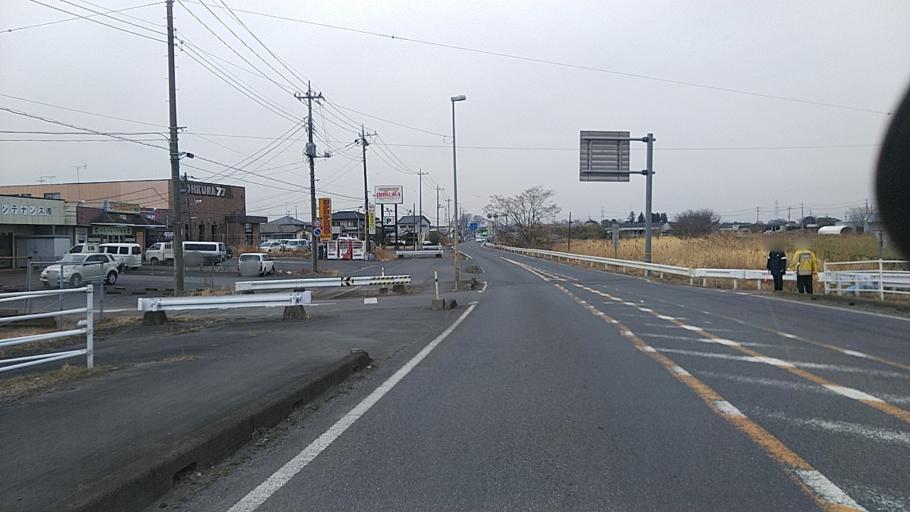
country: JP
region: Ibaraki
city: Yuki
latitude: 36.2450
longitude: 139.9249
